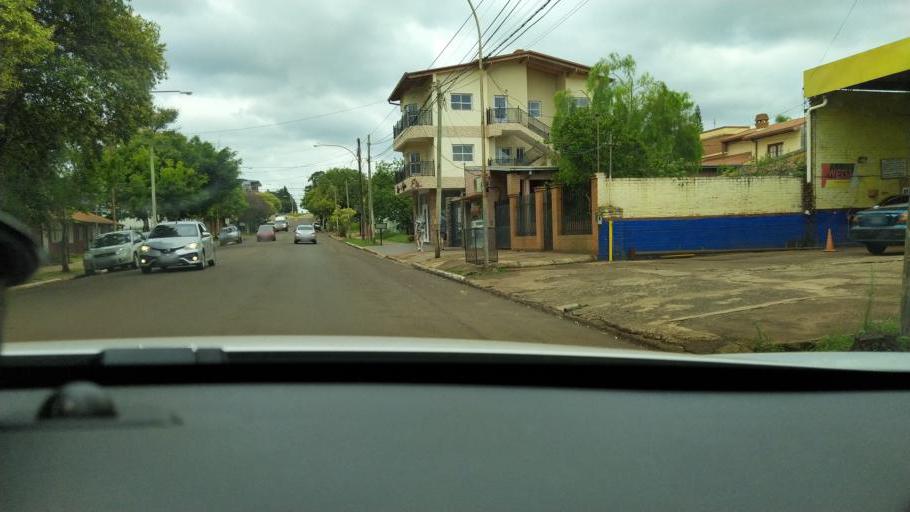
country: AR
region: Misiones
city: Puerto Rico
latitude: -26.8182
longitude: -55.0224
